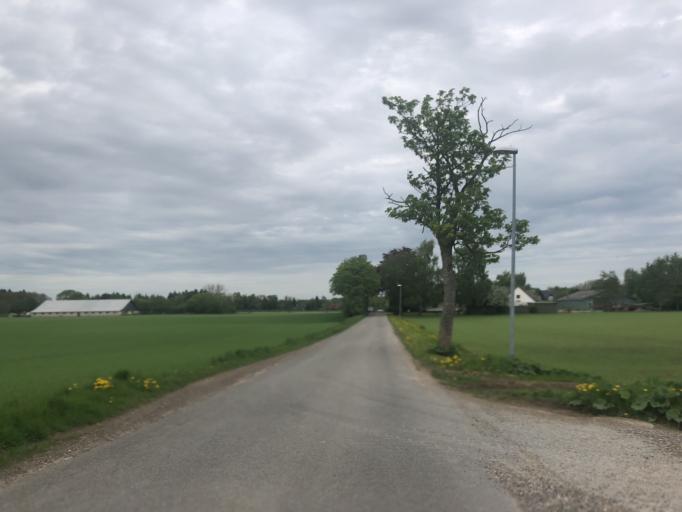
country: DK
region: Zealand
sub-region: Koge Kommune
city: Ejby
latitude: 55.4596
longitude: 12.1036
